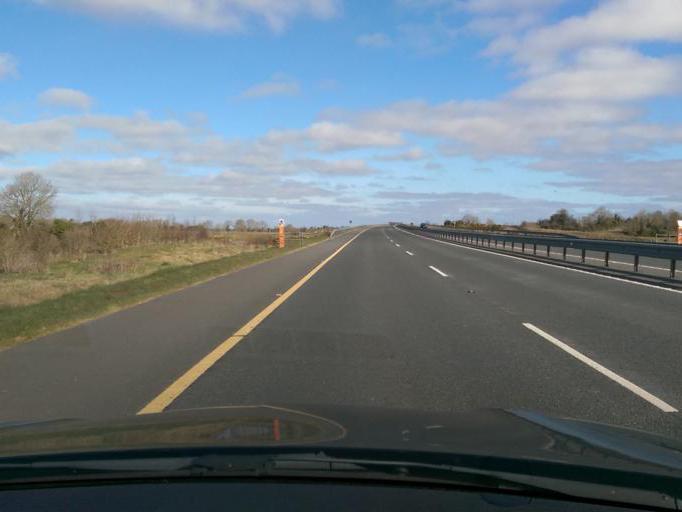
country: IE
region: Leinster
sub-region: An Iarmhi
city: Athlone
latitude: 53.3924
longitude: -8.0498
